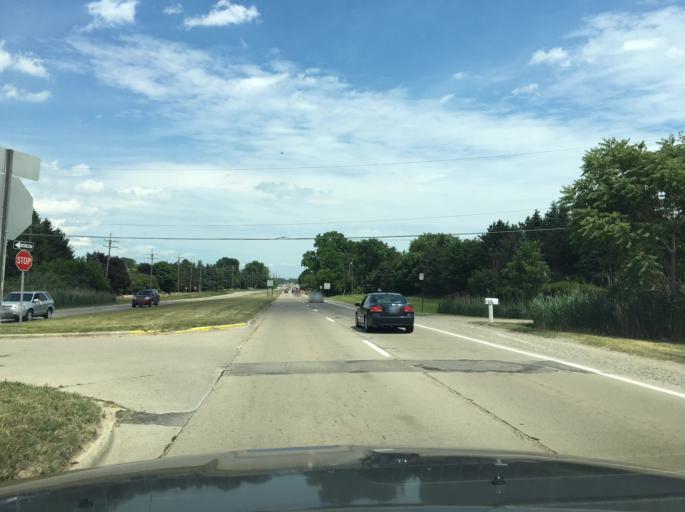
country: US
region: Michigan
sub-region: Macomb County
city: Shelby
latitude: 42.7136
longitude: -83.0470
